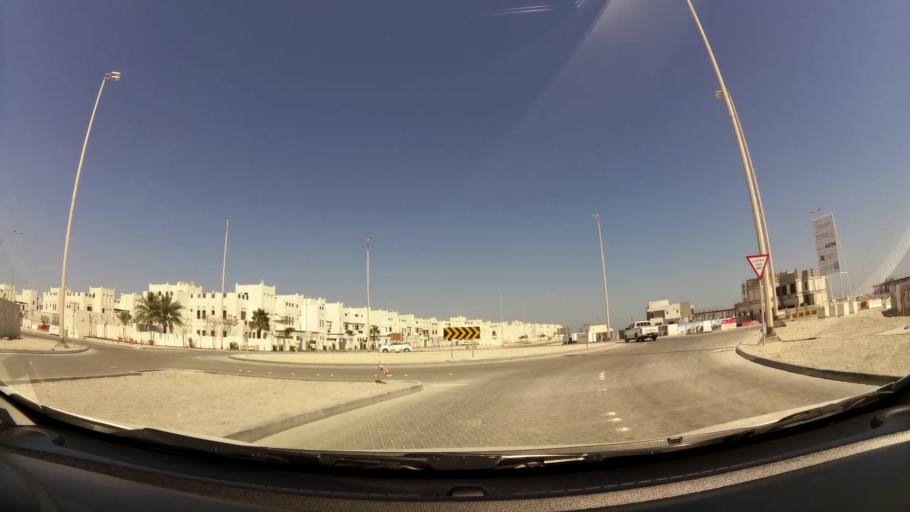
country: BH
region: Muharraq
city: Al Muharraq
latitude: 26.2994
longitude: 50.6377
